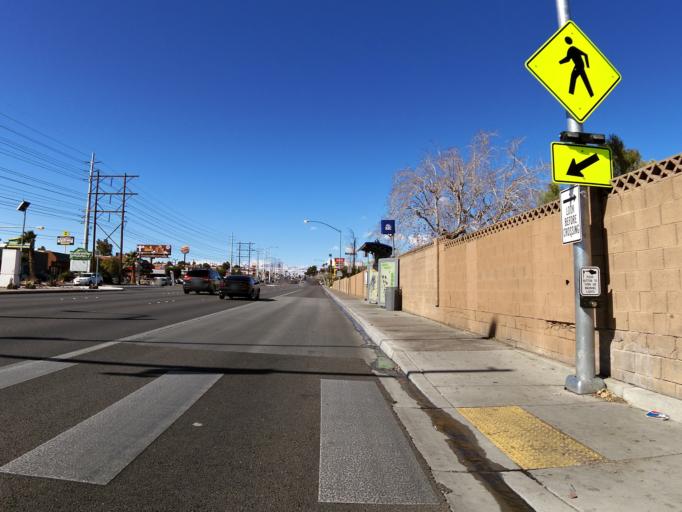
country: US
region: Nevada
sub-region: Clark County
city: Spring Valley
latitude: 36.1156
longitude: -115.2042
